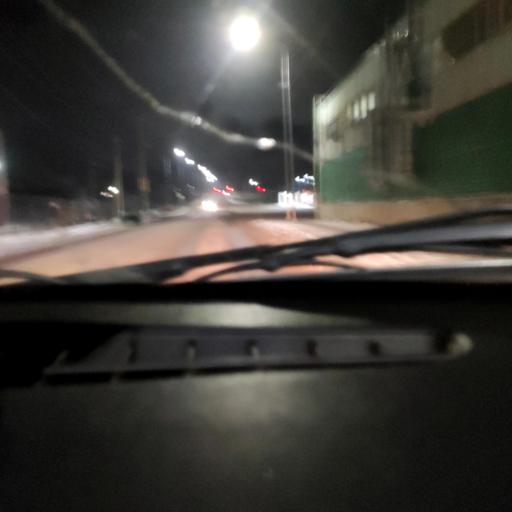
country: RU
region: Bashkortostan
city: Avdon
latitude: 54.6075
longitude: 55.8444
